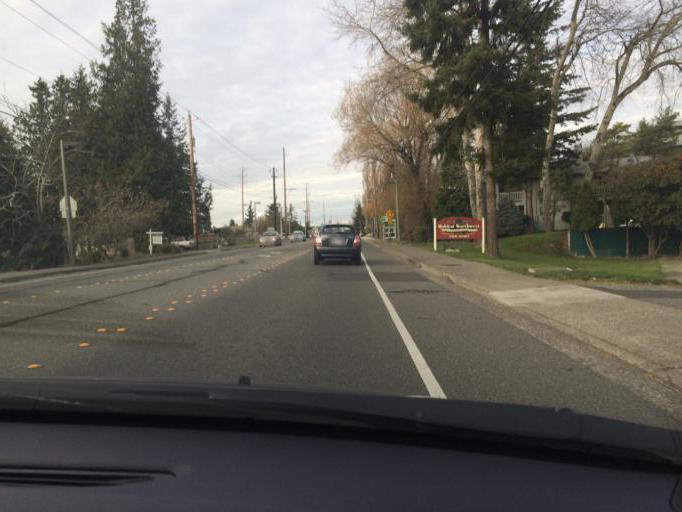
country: US
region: Washington
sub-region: Whatcom County
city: Bellingham
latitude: 48.7809
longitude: -122.5011
